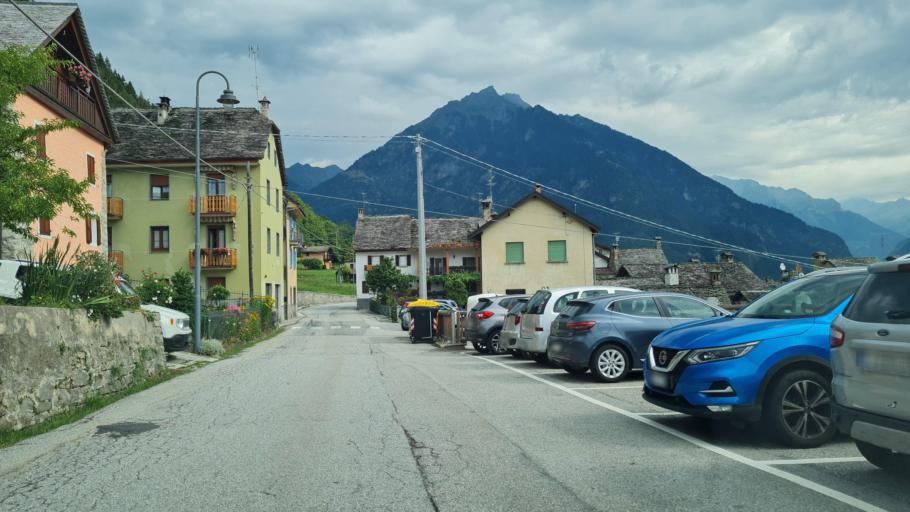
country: IT
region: Piedmont
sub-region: Provincia Verbano-Cusio-Ossola
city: Baceno
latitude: 46.2403
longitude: 8.3132
